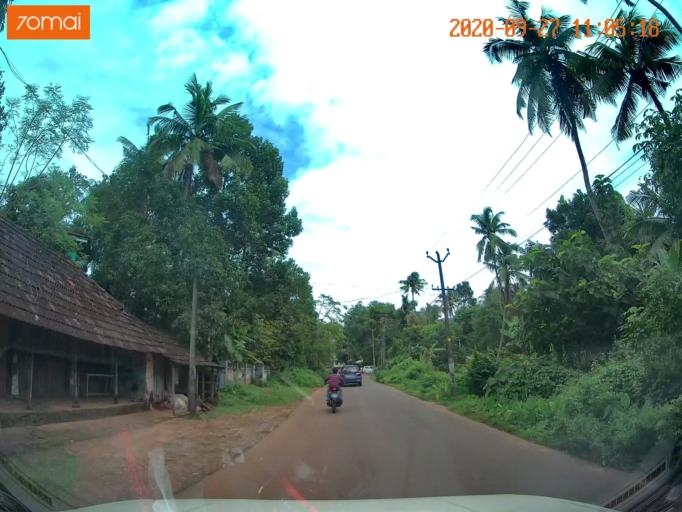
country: IN
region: Kerala
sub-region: Thrissur District
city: Irinjalakuda
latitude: 10.4233
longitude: 76.2483
